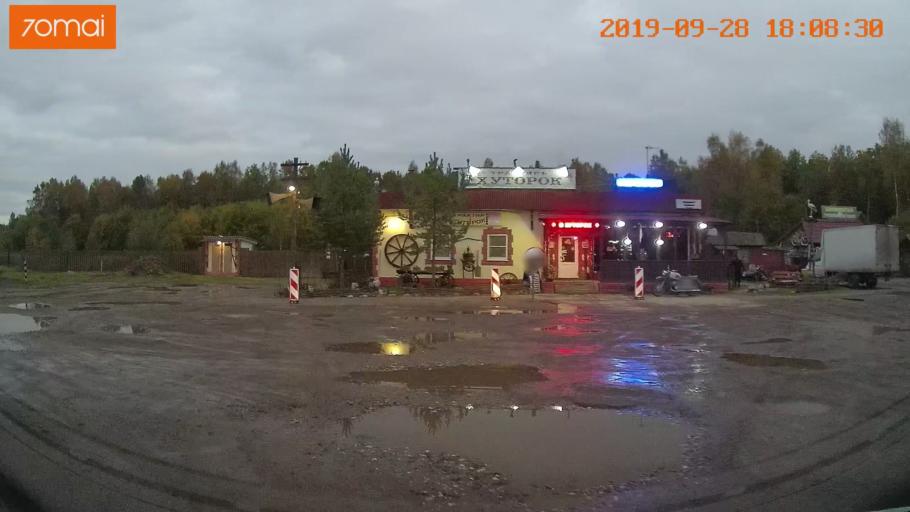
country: RU
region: Jaroslavl
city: Gavrilov-Yam
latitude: 57.2704
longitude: 39.9583
